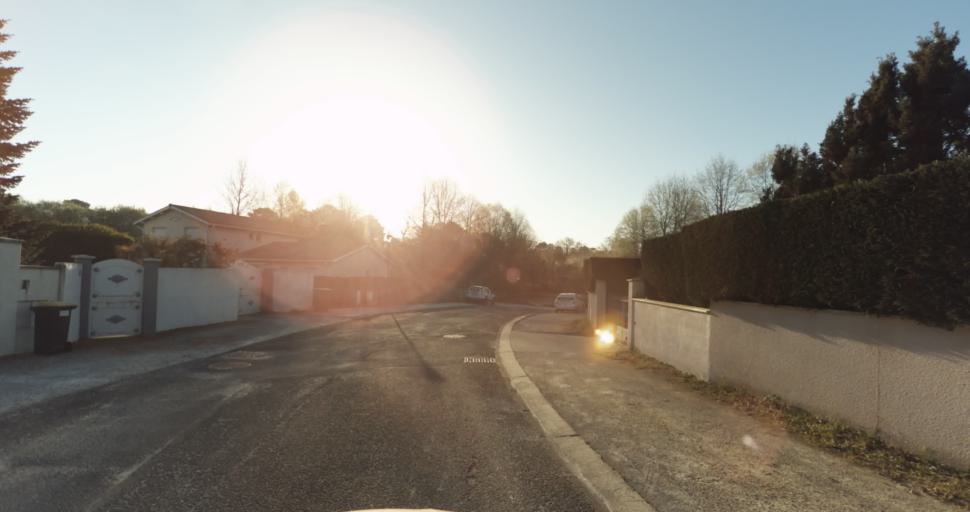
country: FR
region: Aquitaine
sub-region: Departement de la Gironde
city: Martignas-sur-Jalle
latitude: 44.8151
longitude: -0.7766
